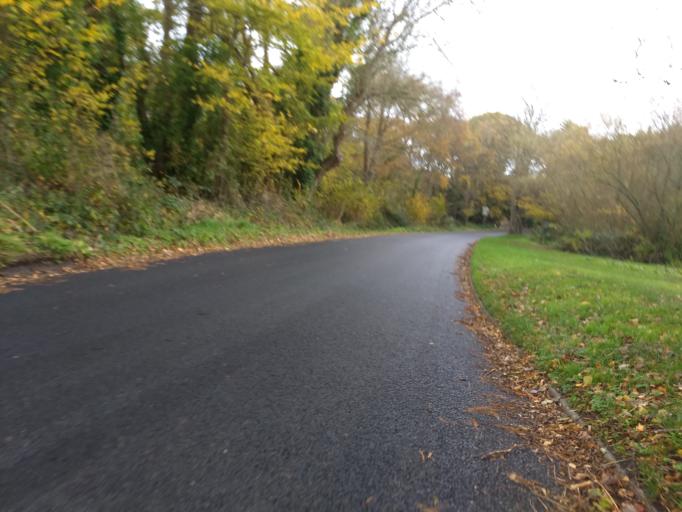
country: GB
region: England
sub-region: Isle of Wight
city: Freshwater
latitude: 50.6756
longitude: -1.5118
